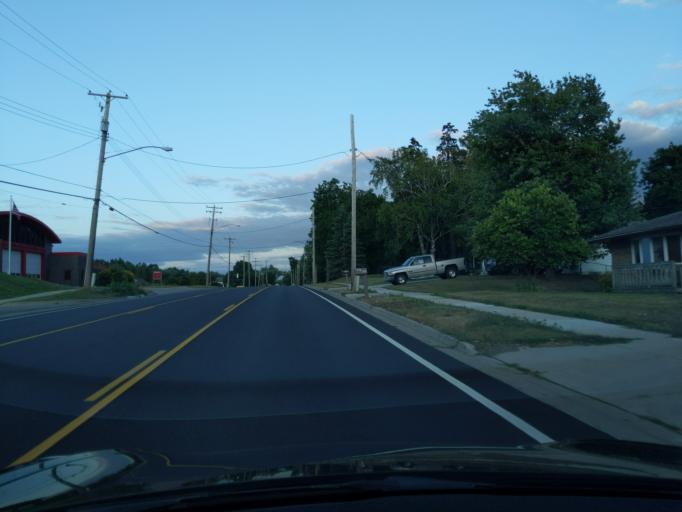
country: US
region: Michigan
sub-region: Ingham County
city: Holt
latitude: 42.6692
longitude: -84.5324
